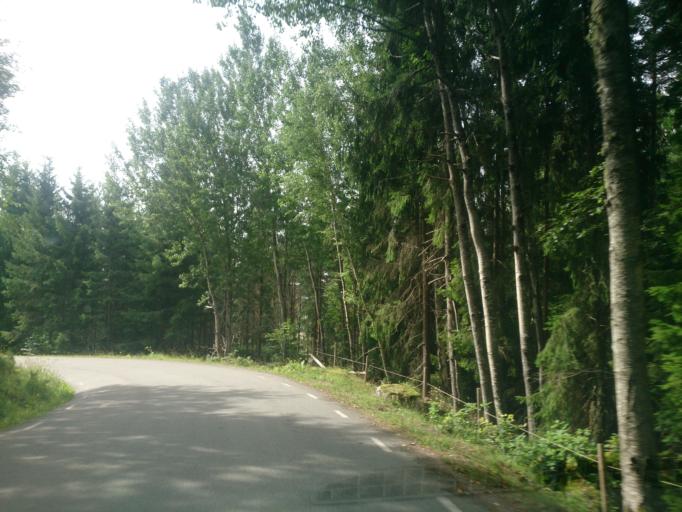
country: SE
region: OEstergoetland
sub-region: Atvidabergs Kommun
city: Atvidaberg
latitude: 58.2860
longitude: 16.0958
